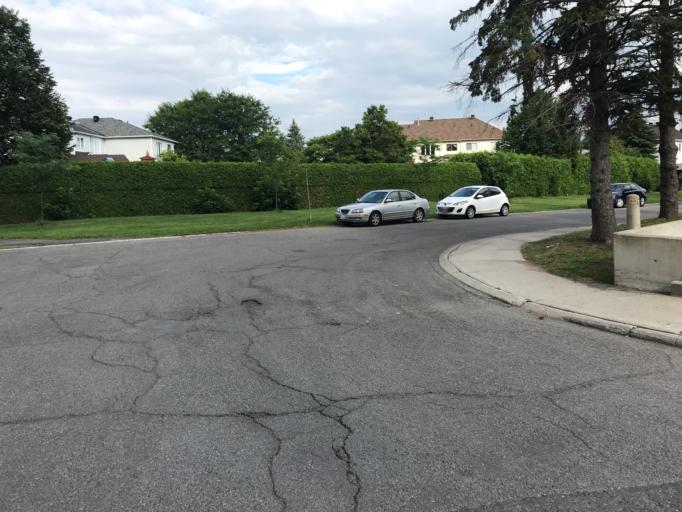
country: CA
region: Ontario
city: Ottawa
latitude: 45.4297
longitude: -75.6200
